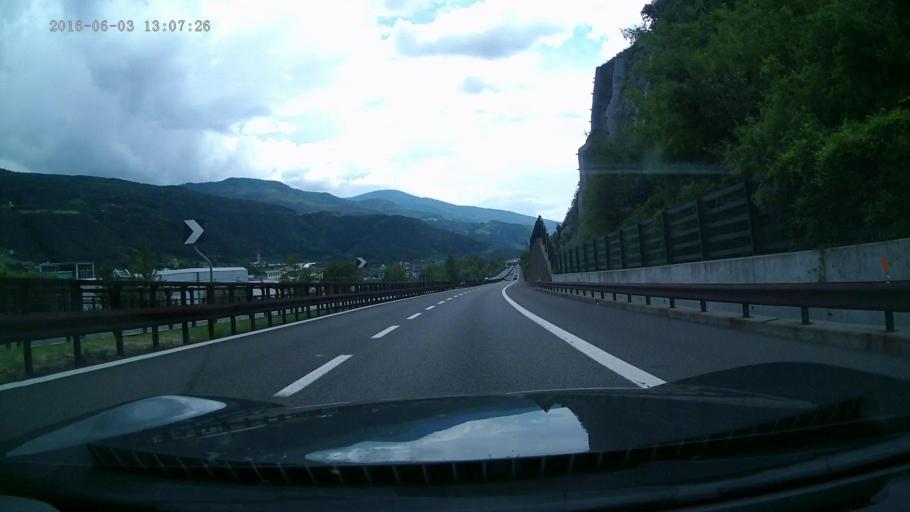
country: IT
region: Trentino-Alto Adige
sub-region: Bolzano
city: Bressanone
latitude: 46.7018
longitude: 11.6469
